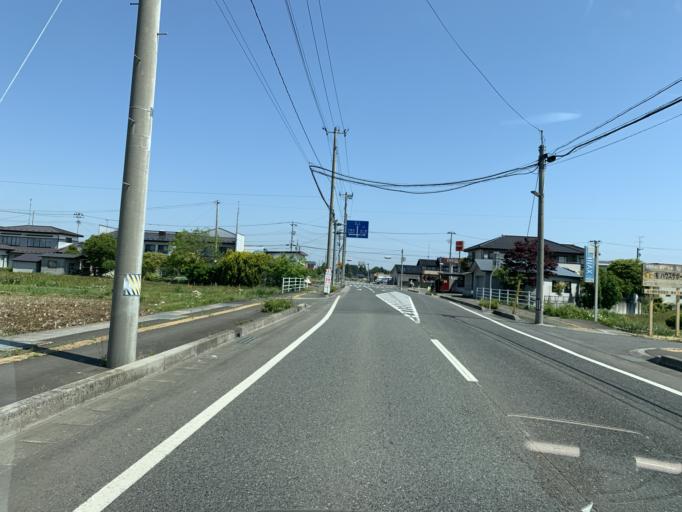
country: JP
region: Iwate
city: Mizusawa
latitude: 39.1951
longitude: 141.0951
